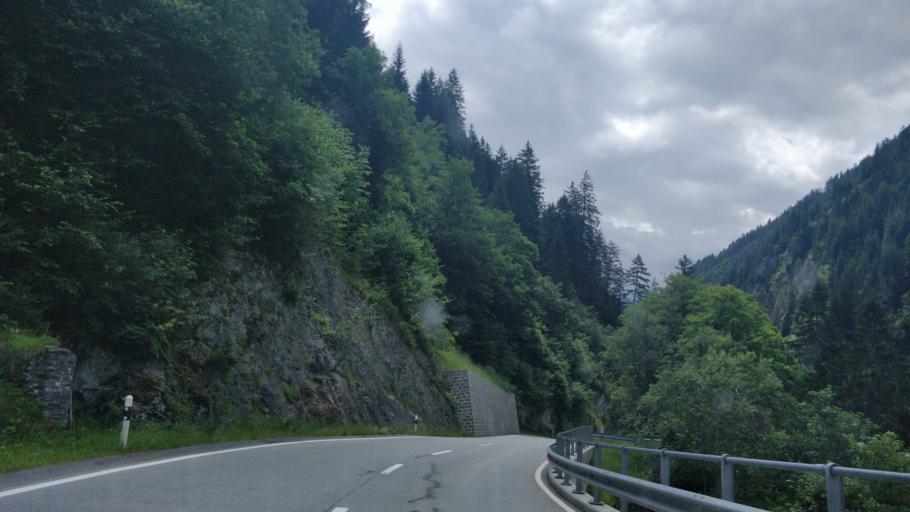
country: CH
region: Grisons
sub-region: Hinterrhein District
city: Hinterrhein
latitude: 46.6521
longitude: 9.1872
